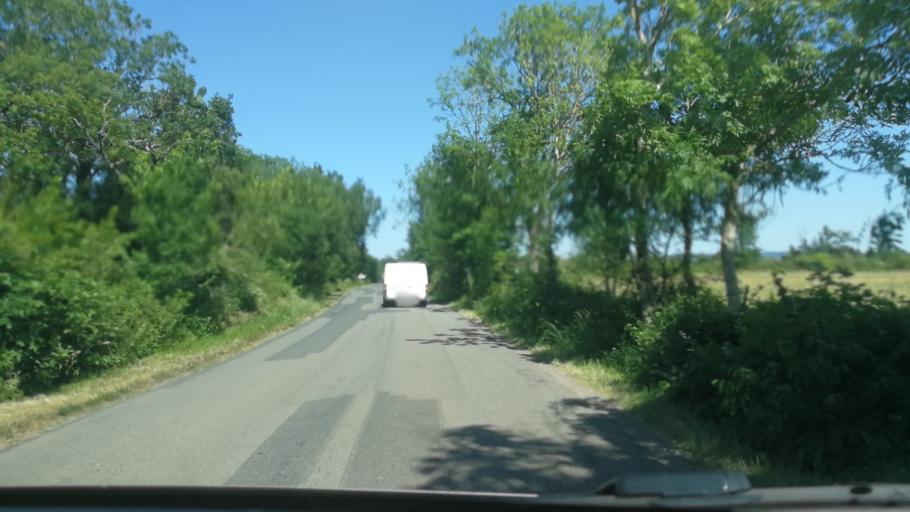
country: FR
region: Midi-Pyrenees
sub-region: Departement de l'Aveyron
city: Sebazac-Concoures
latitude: 44.4112
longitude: 2.5876
